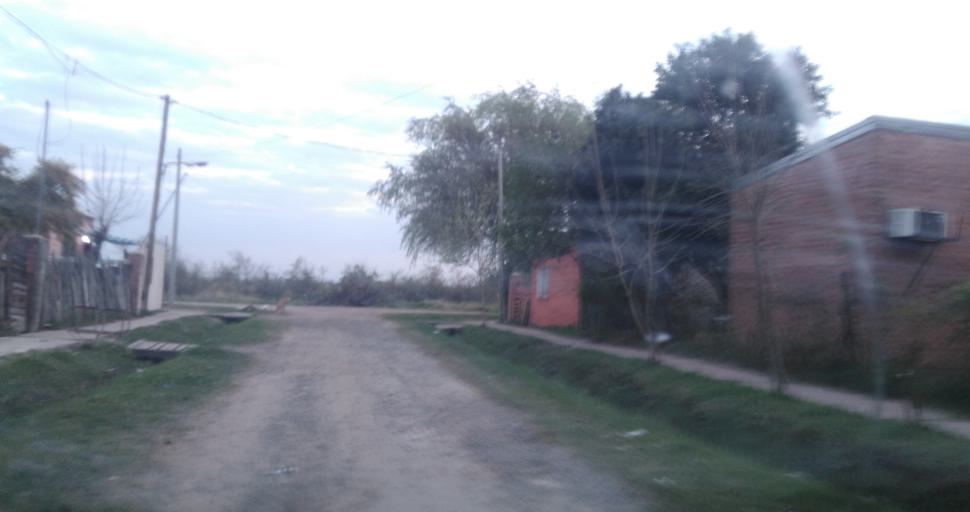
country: AR
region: Chaco
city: Fontana
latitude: -27.4469
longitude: -59.0404
